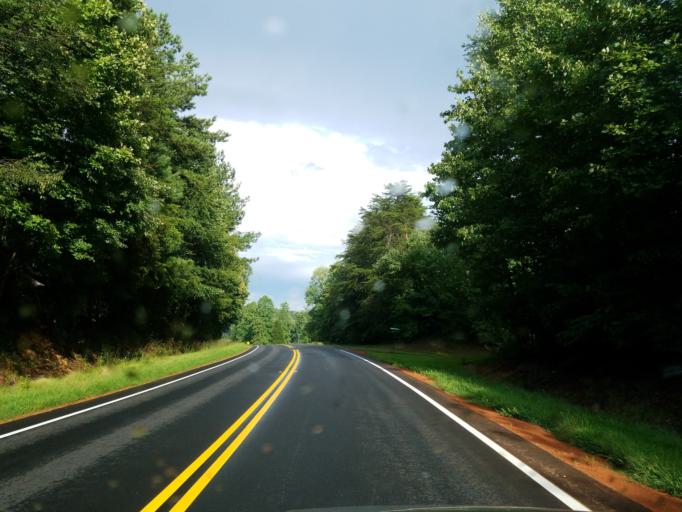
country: US
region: Georgia
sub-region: White County
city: Cleveland
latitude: 34.6131
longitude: -83.7852
